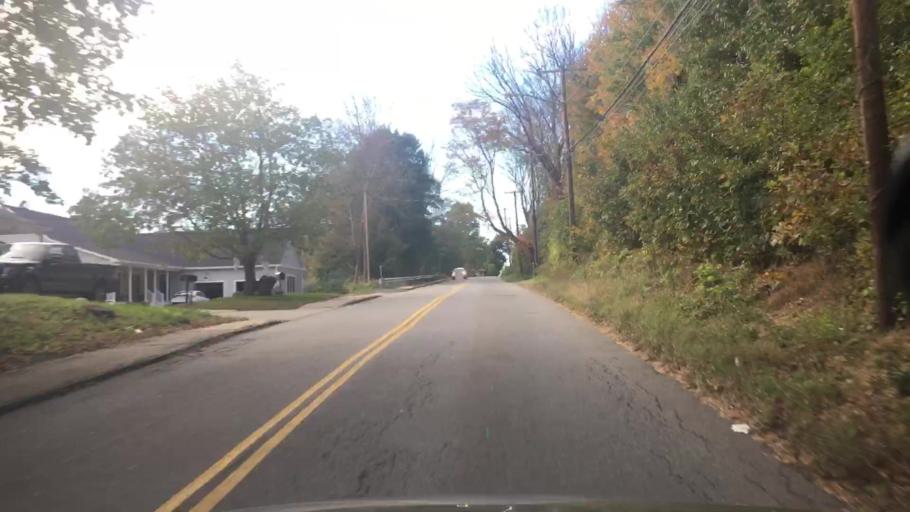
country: US
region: Massachusetts
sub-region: Worcester County
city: Charlton
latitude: 42.1376
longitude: -71.9719
